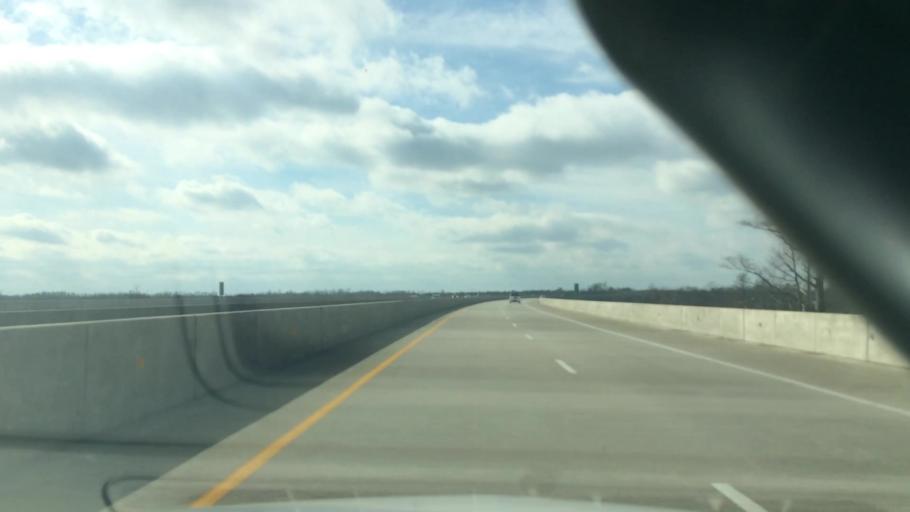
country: US
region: North Carolina
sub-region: Brunswick County
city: Navassa
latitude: 34.2748
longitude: -77.9876
